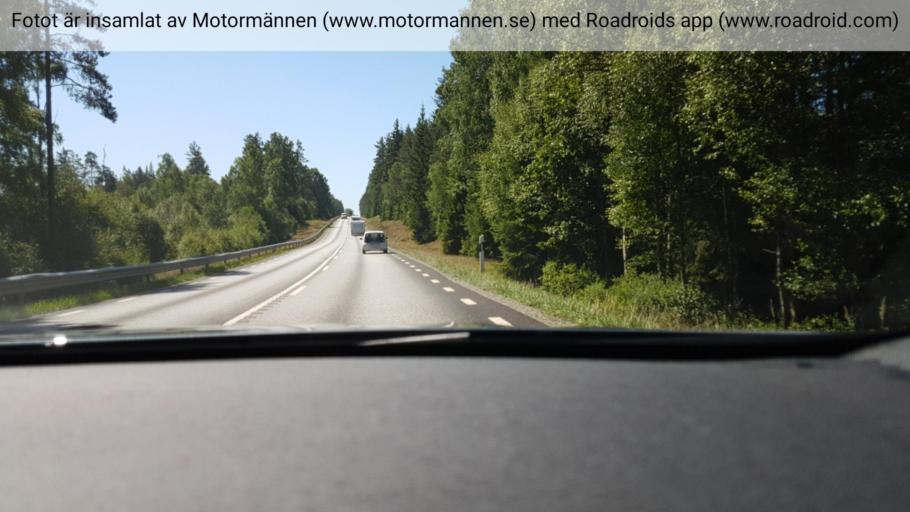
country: SE
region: Joenkoeping
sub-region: Gnosjo Kommun
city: Gnosjoe
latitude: 57.5505
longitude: 13.6911
